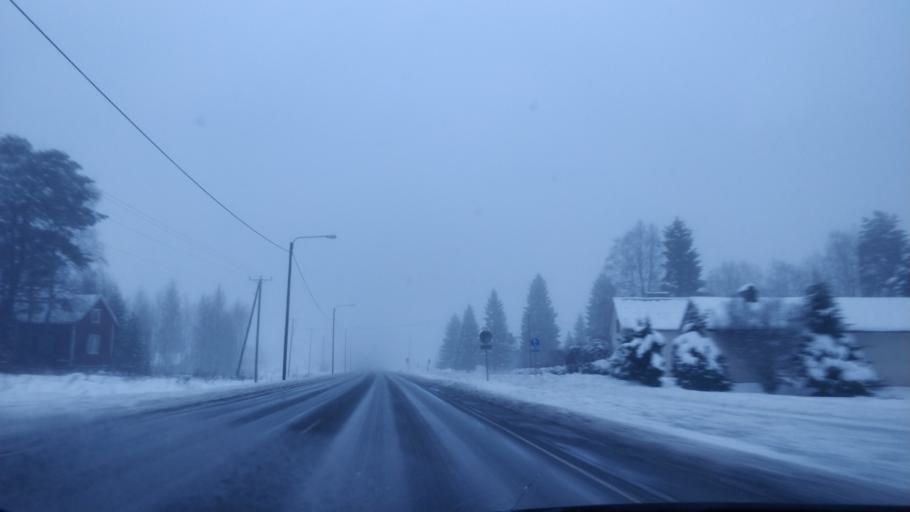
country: FI
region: Lapland
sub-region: Kemi-Tornio
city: Tervola
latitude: 66.1384
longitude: 24.9375
